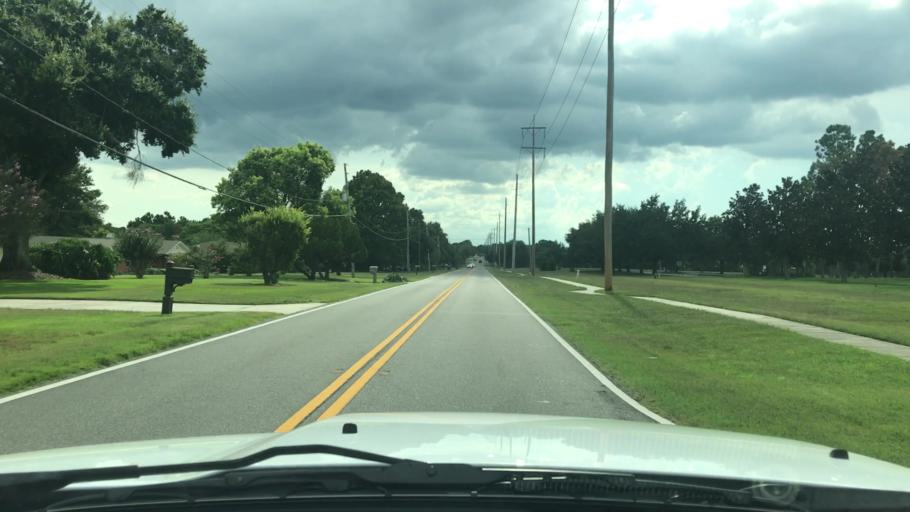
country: US
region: Florida
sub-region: Polk County
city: Cypress Gardens
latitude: 28.0151
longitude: -81.6639
